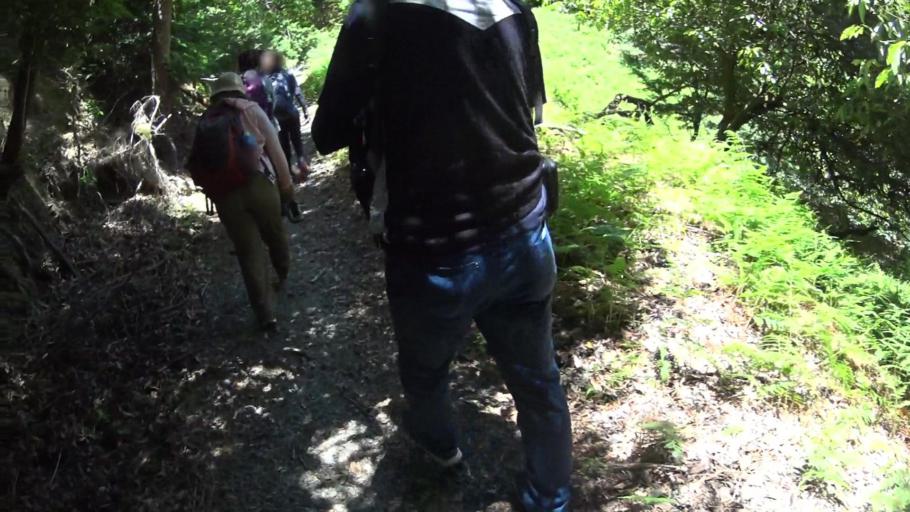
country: JP
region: Kyoto
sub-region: Kyoto-shi
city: Kamigyo-ku
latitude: 35.0524
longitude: 135.8154
